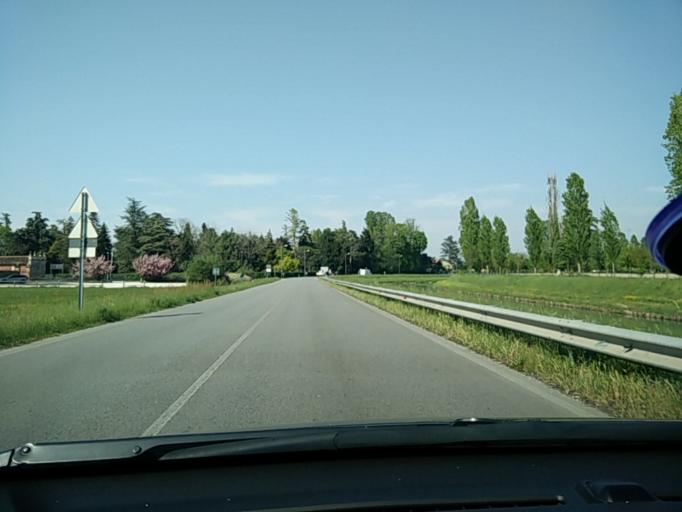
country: IT
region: Veneto
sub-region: Provincia di Venezia
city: Stra
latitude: 45.4098
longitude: 12.0140
